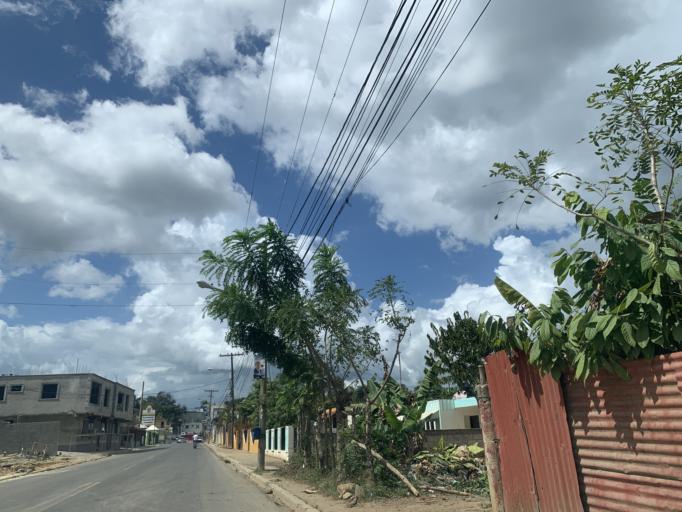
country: DO
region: Monte Plata
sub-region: Yamasa
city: Yamasa
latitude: 18.7651
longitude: -70.0203
